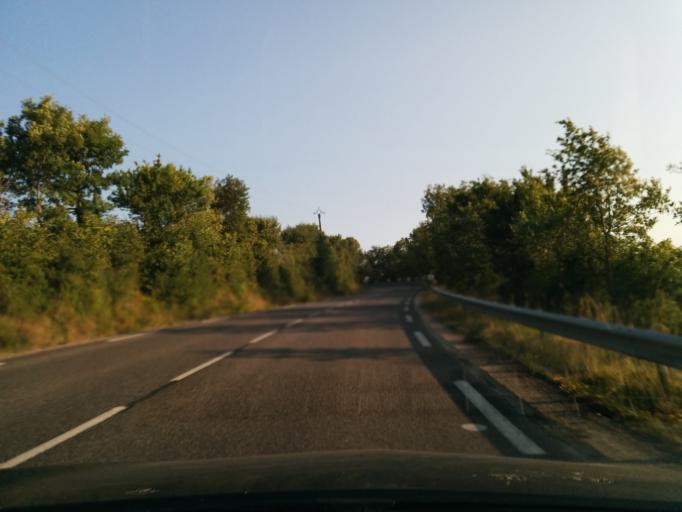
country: FR
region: Midi-Pyrenees
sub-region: Departement du Lot
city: Le Vigan
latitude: 44.6476
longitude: 1.4798
